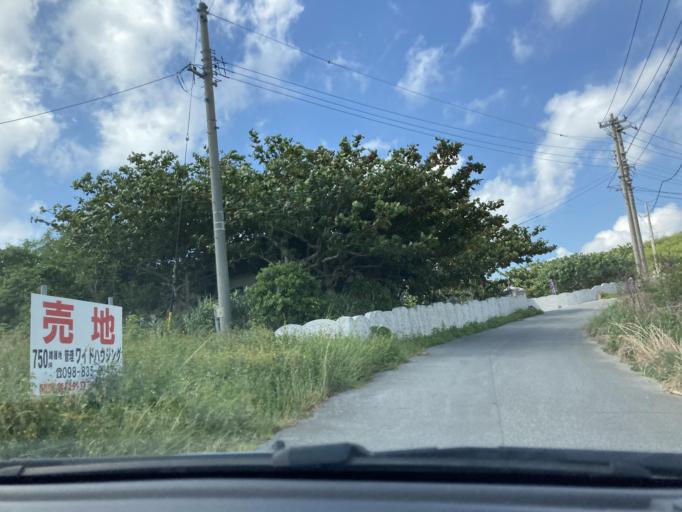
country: JP
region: Okinawa
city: Itoman
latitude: 26.0999
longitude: 127.7304
